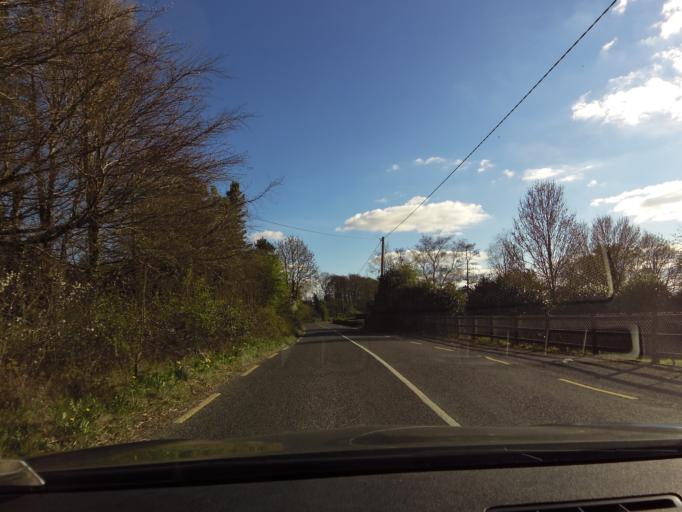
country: IE
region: Connaught
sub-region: County Galway
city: Portumna
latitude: 53.0923
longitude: -8.1844
